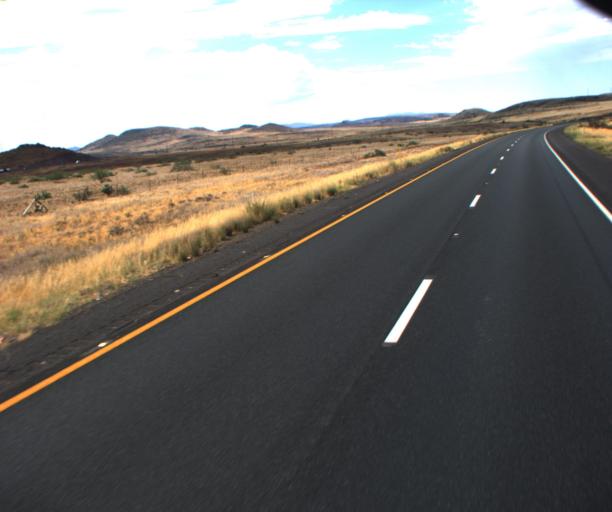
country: US
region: Arizona
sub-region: Yavapai County
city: Cordes Lakes
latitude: 34.4515
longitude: -112.0349
